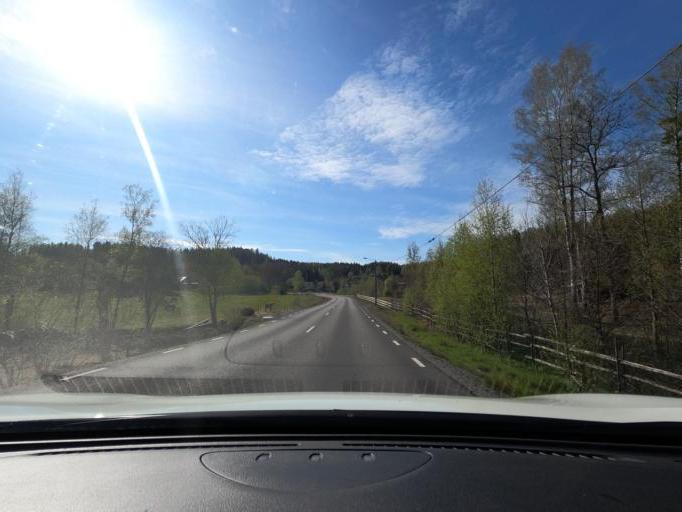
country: SE
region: Vaestra Goetaland
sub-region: Harryda Kommun
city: Landvetter
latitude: 57.6161
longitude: 12.2878
